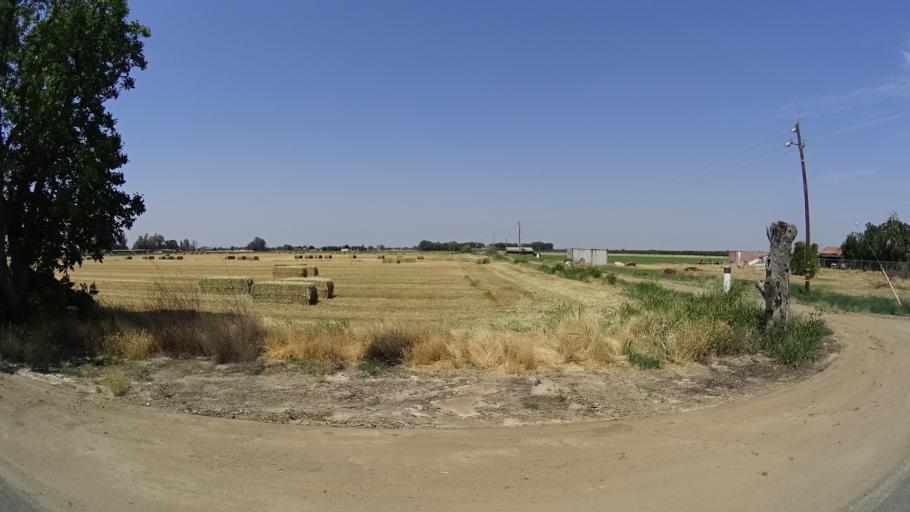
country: US
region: California
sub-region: Kings County
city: Armona
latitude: 36.3189
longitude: -119.7448
